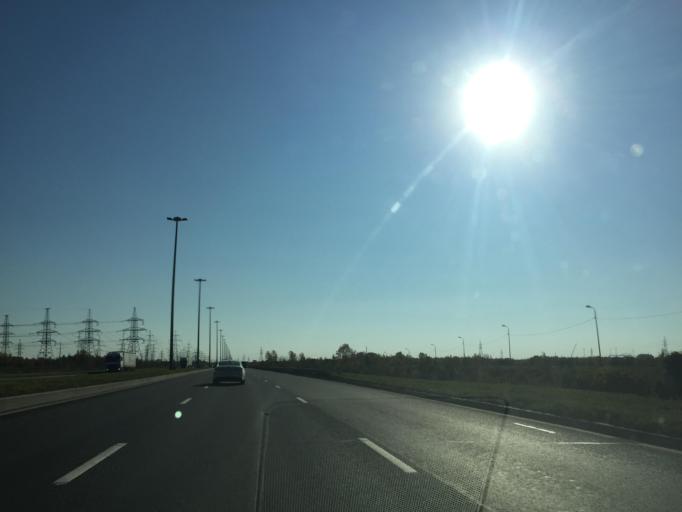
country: RU
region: St.-Petersburg
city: Petro-Slavyanka
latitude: 59.7654
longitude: 30.5036
